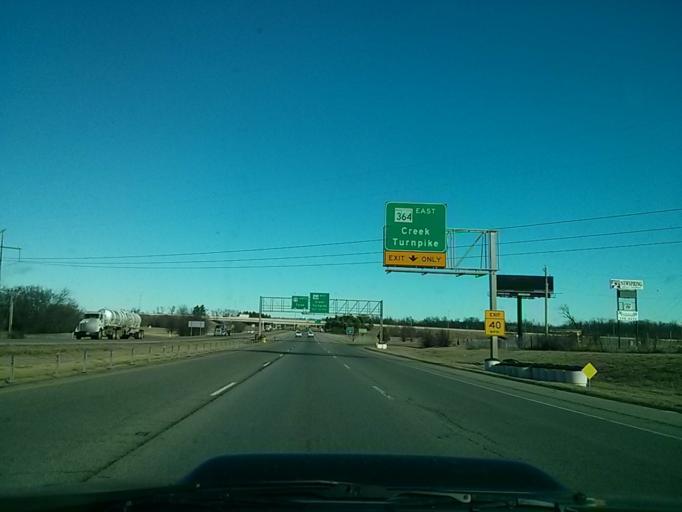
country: US
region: Oklahoma
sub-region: Tulsa County
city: Jenks
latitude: 36.0052
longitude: -96.0115
